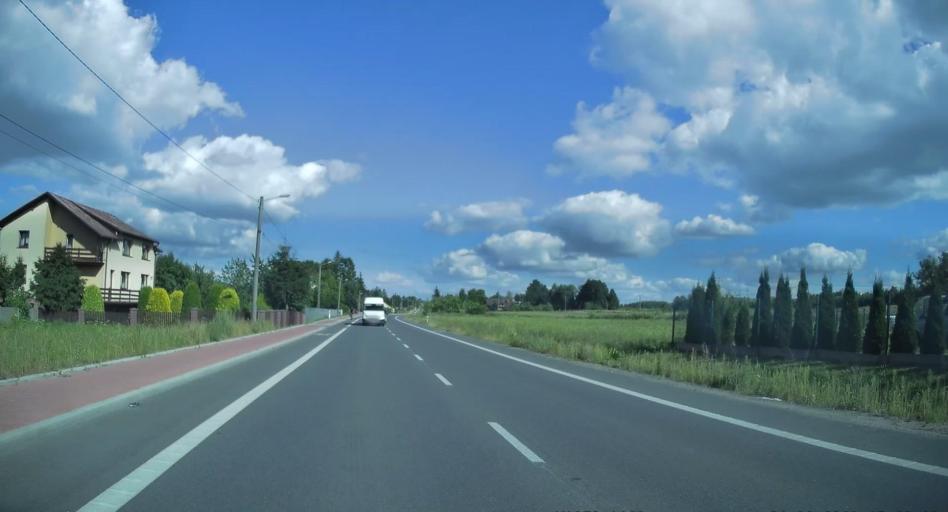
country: PL
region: Swietokrzyskie
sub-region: Powiat kielecki
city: Bodzentyn
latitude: 50.9360
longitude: 20.9591
